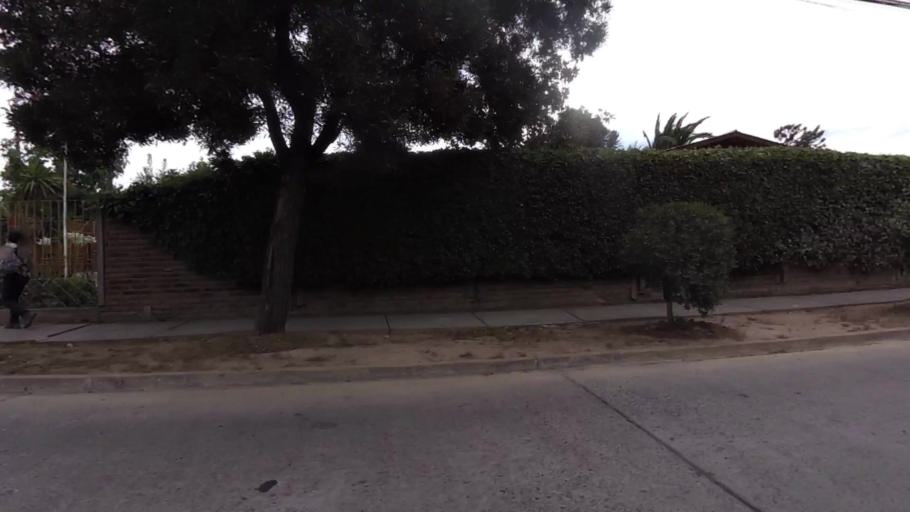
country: CL
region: O'Higgins
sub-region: Provincia de Cachapoal
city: Rancagua
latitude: -34.1505
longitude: -70.7398
